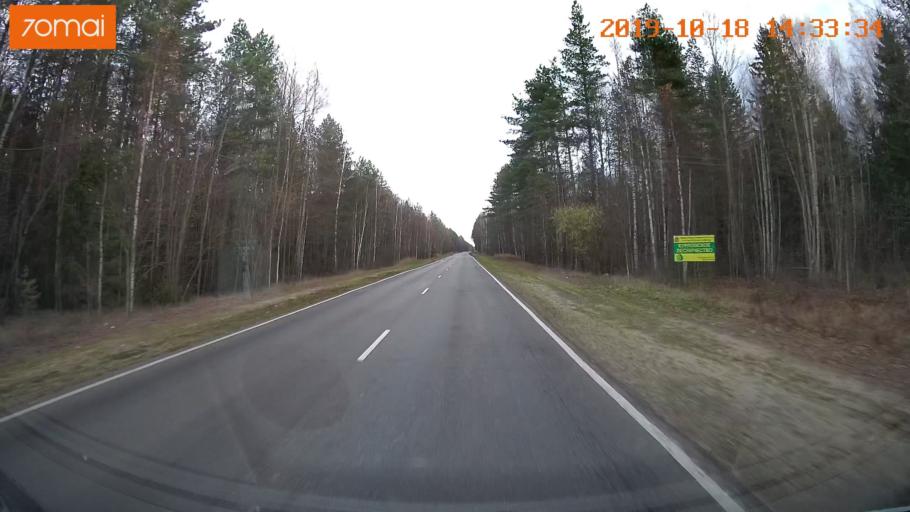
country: RU
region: Rjazan
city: Tuma
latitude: 55.2028
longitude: 40.5992
